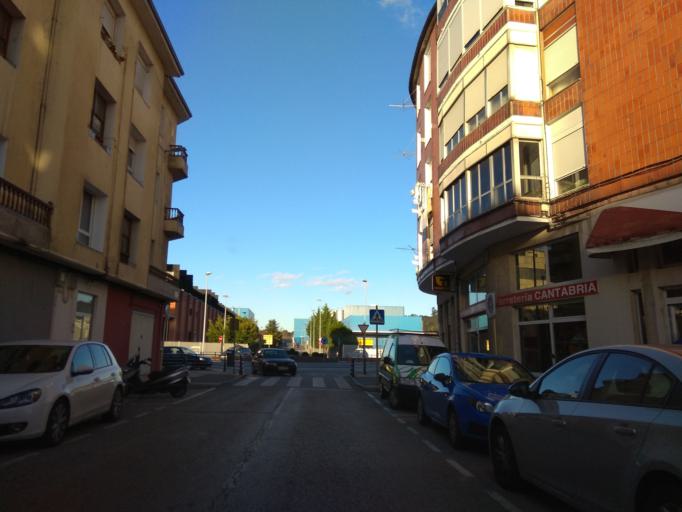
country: ES
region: Cantabria
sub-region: Provincia de Cantabria
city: Torrelavega
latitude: 43.3529
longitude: -4.0524
